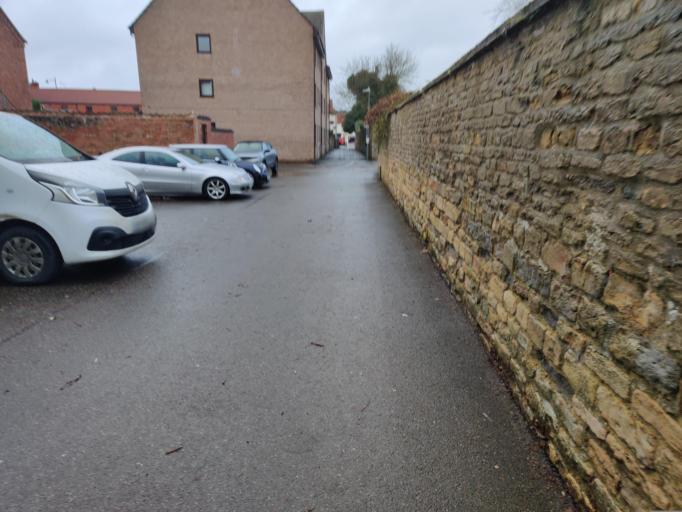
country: GB
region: England
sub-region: Lincolnshire
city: Bourne
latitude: 52.7667
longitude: -0.3760
